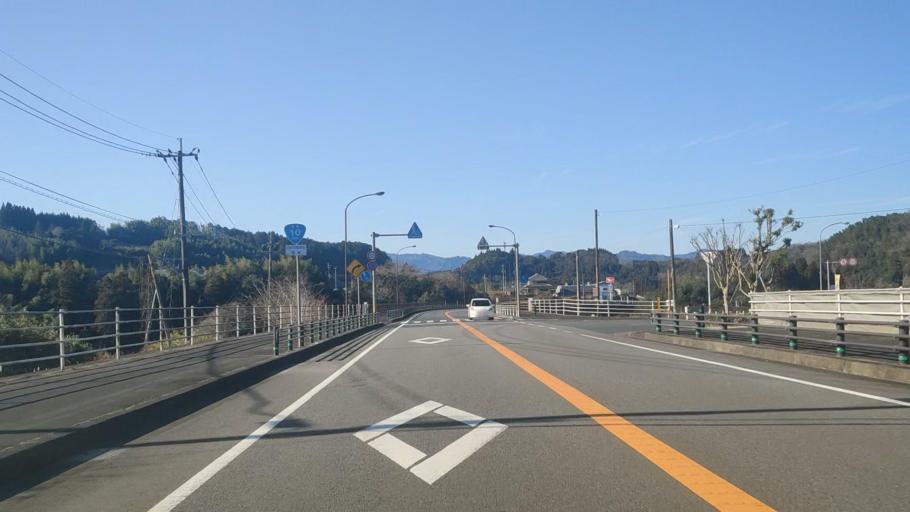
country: JP
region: Oita
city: Usuki
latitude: 33.0572
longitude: 131.6756
